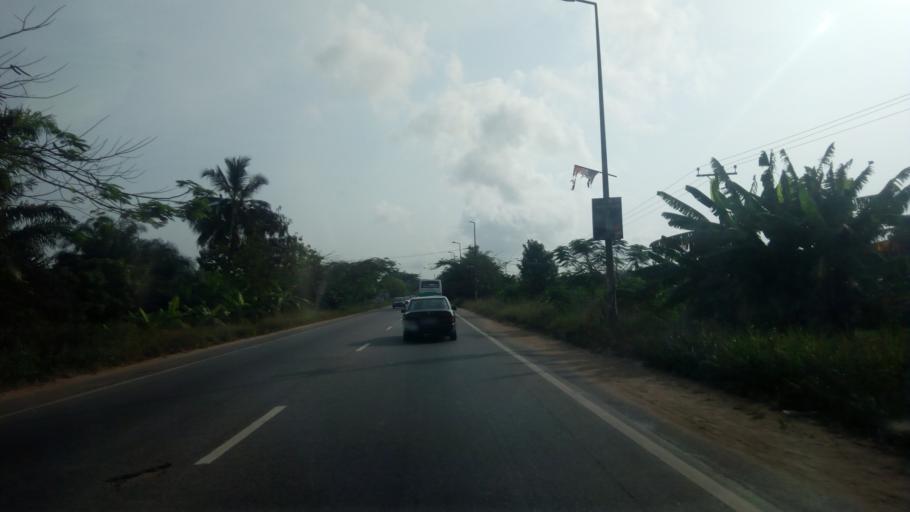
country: GH
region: Central
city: Cape Coast
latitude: 5.1188
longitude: -1.2758
